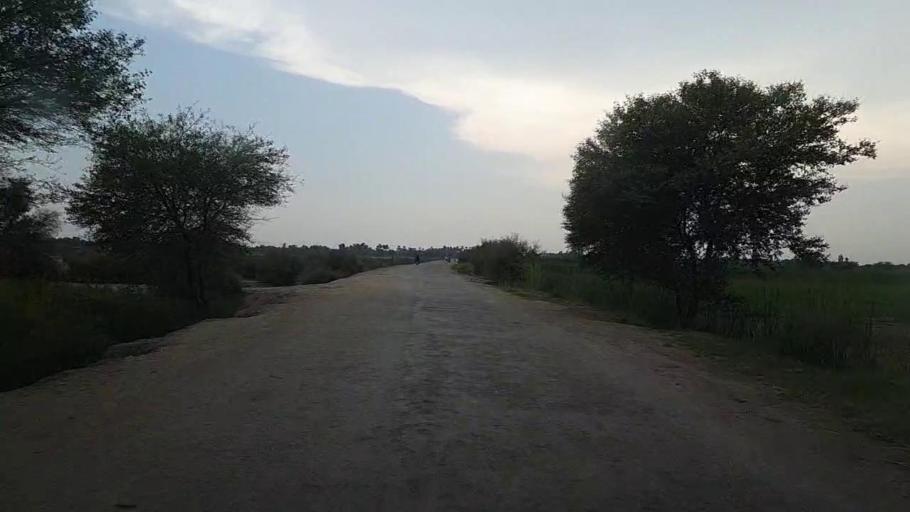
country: PK
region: Sindh
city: Khanpur
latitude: 27.8388
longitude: 69.4785
